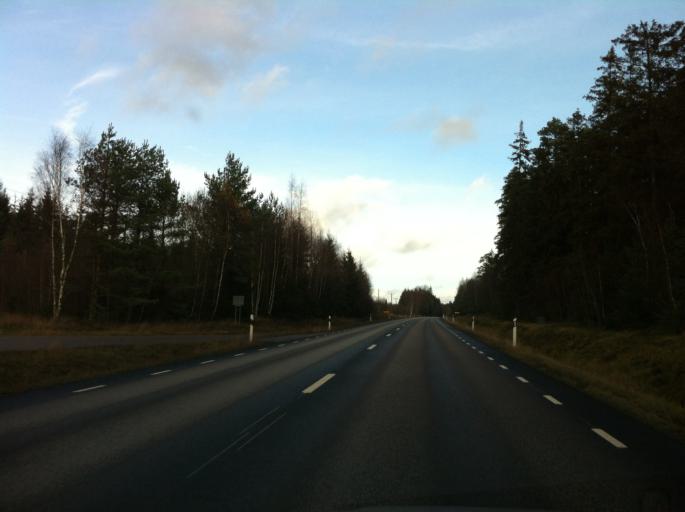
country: SE
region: Kronoberg
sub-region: Almhults Kommun
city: AElmhult
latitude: 56.5784
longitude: 14.1882
